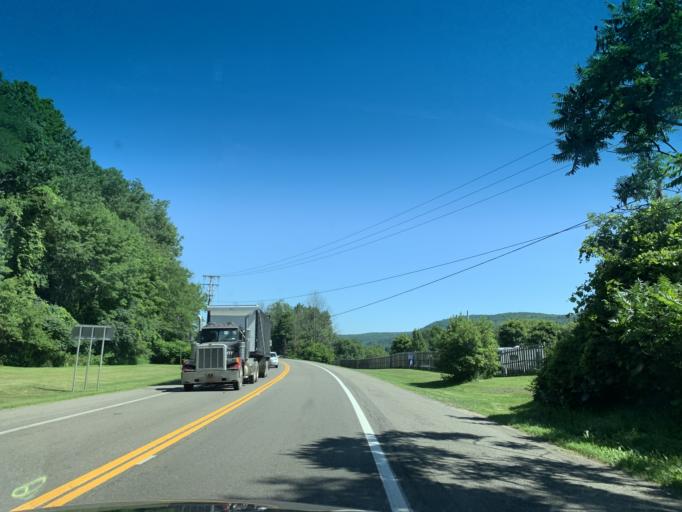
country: US
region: New York
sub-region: Delaware County
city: Sidney
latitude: 42.3419
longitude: -75.4022
